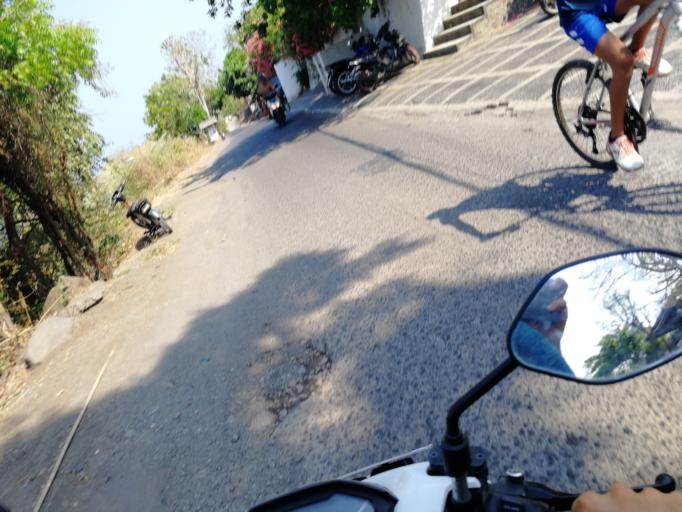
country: ID
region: Bali
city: Biaslantang Kaler
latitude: -8.3456
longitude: 115.6762
